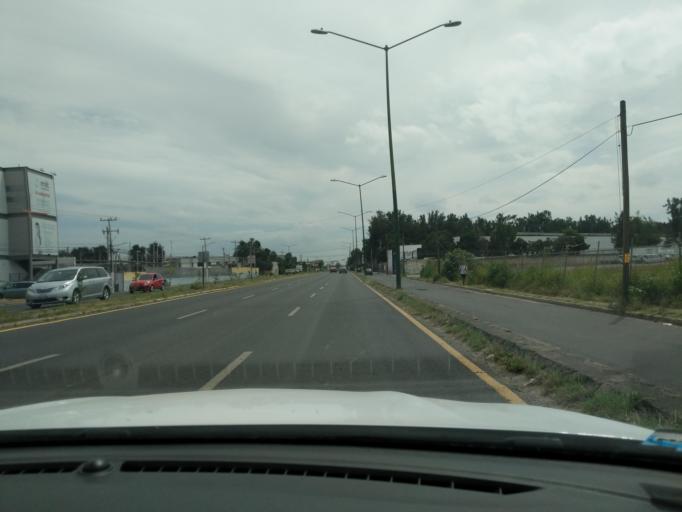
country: MX
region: Jalisco
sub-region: Zapopan
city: Puerta del Llano
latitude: 20.7881
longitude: -103.4722
